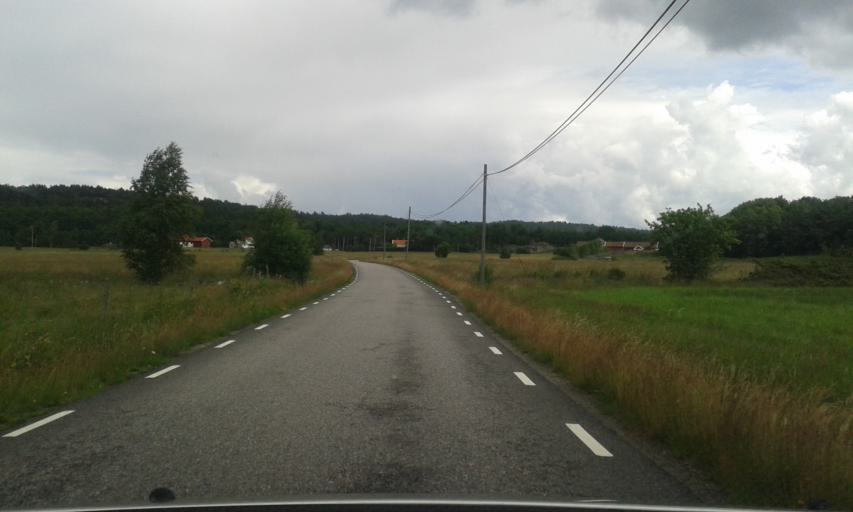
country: SE
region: Vaestra Goetaland
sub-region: Kungalvs Kommun
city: Kode
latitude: 57.9438
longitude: 11.9149
